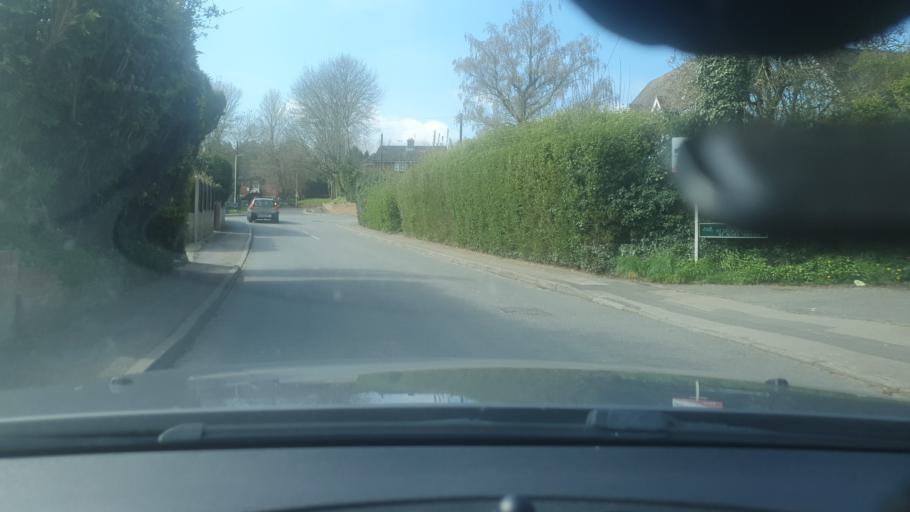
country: GB
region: England
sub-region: West Berkshire
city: Lambourn
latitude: 51.5061
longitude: -1.5289
